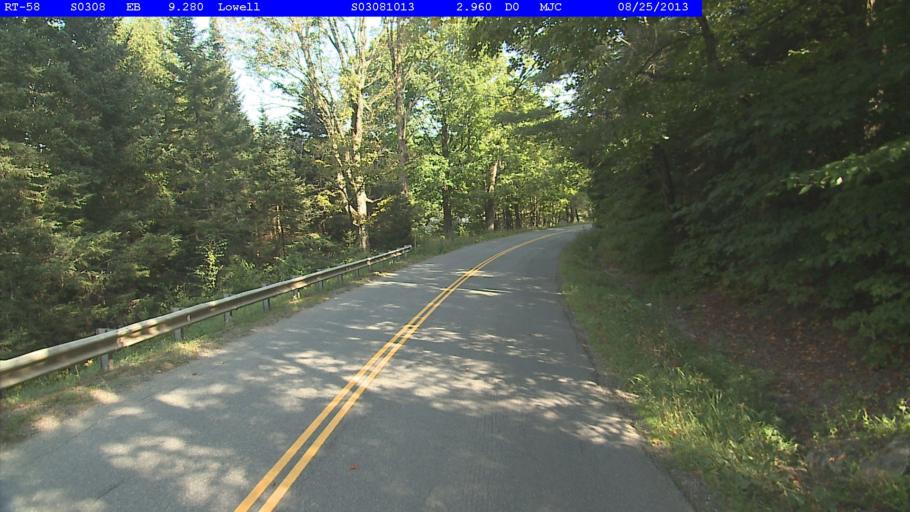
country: US
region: Vermont
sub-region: Lamoille County
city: Hyde Park
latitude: 44.8110
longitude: -72.4614
